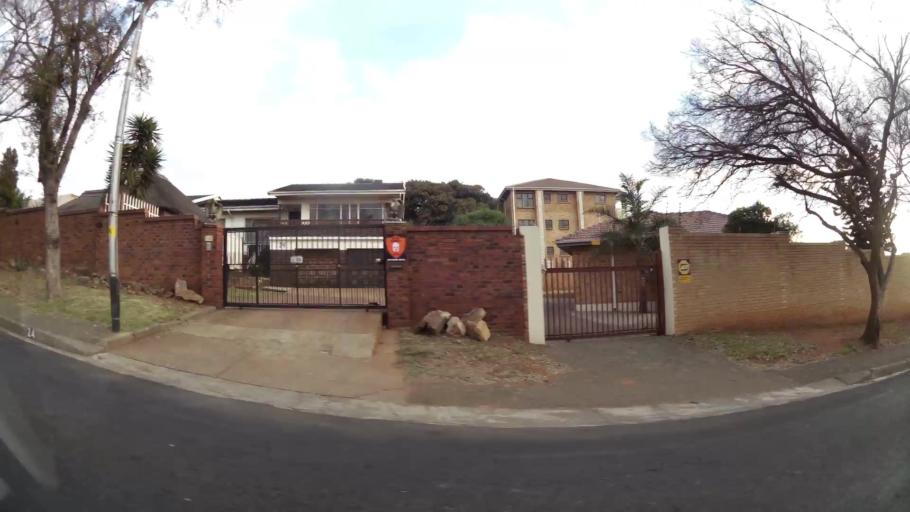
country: ZA
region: Gauteng
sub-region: Ekurhuleni Metropolitan Municipality
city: Germiston
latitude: -26.1671
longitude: 28.1818
